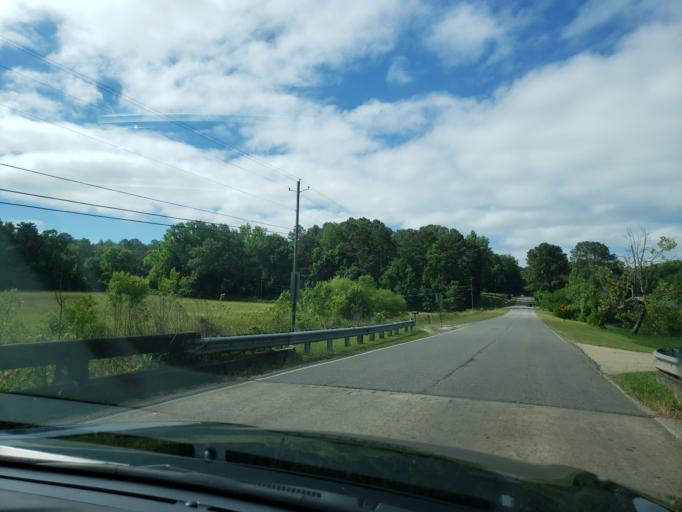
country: US
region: Alabama
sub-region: Calhoun County
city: Weaver
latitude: 33.7385
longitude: -85.8475
